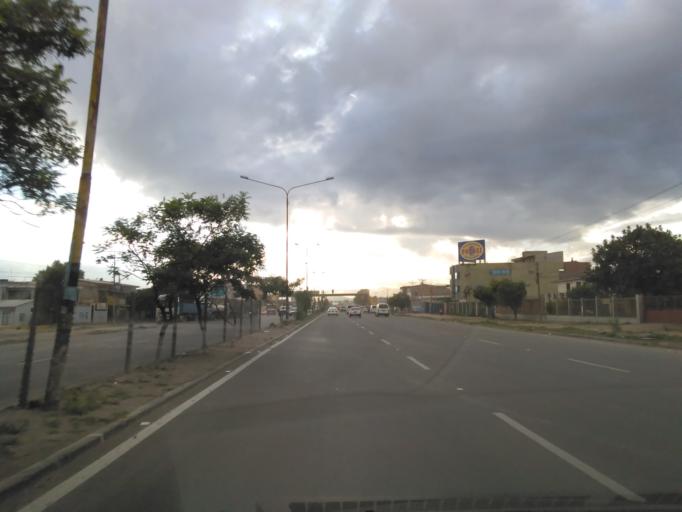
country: BO
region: Cochabamba
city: Cochabamba
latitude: -17.3916
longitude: -66.2237
